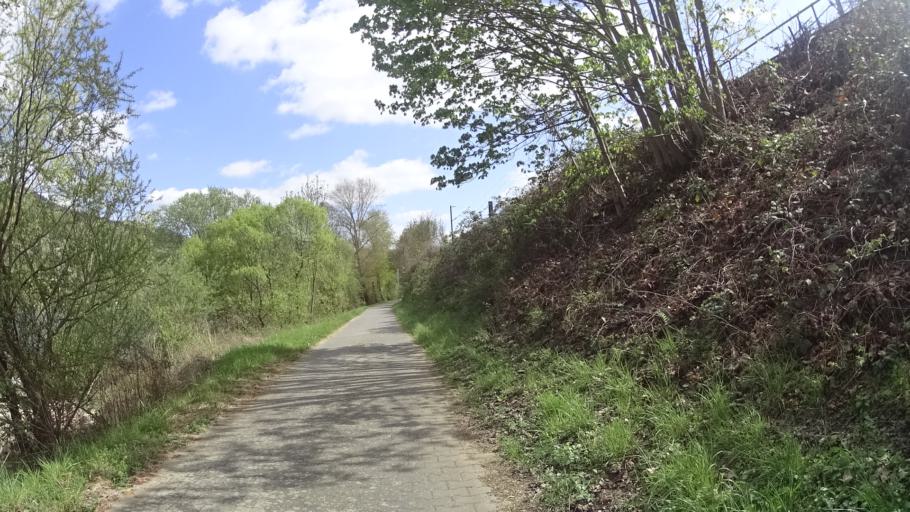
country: DE
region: Rheinland-Pfalz
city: Niederheimbach
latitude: 50.0237
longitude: 7.8231
